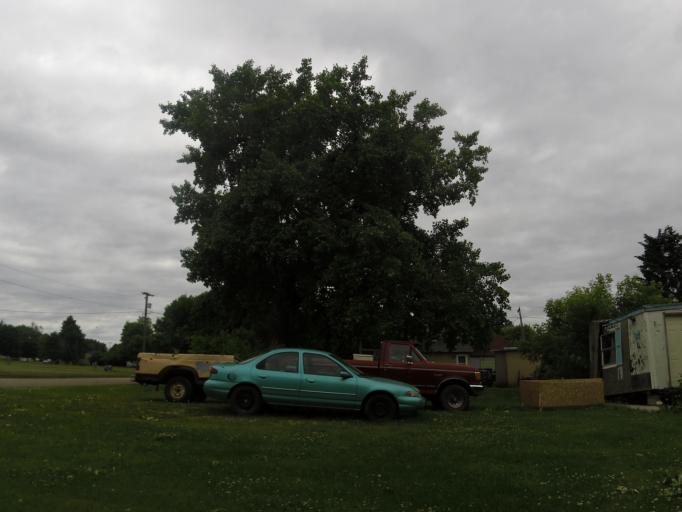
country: US
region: North Dakota
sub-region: Walsh County
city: Grafton
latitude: 48.6173
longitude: -97.4434
